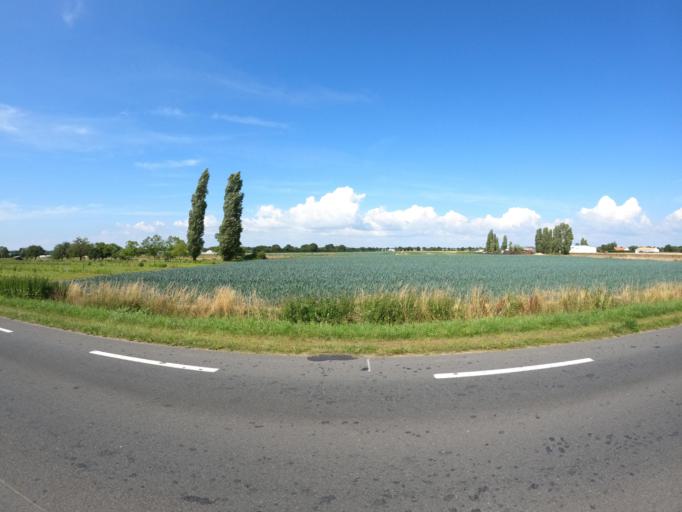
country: FR
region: Pays de la Loire
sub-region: Departement de la Loire-Atlantique
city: Machecoul
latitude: 46.9917
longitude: -1.8001
